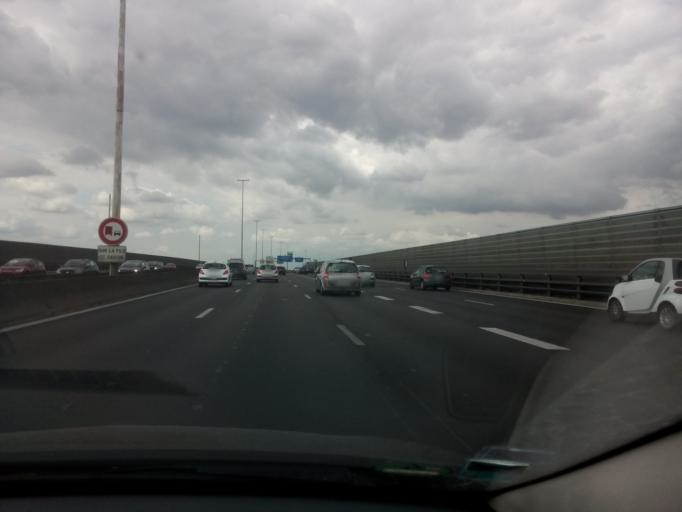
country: FR
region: Ile-de-France
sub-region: Departement de Seine-Saint-Denis
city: Noisy-le-Sec
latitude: 48.8943
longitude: 2.4720
